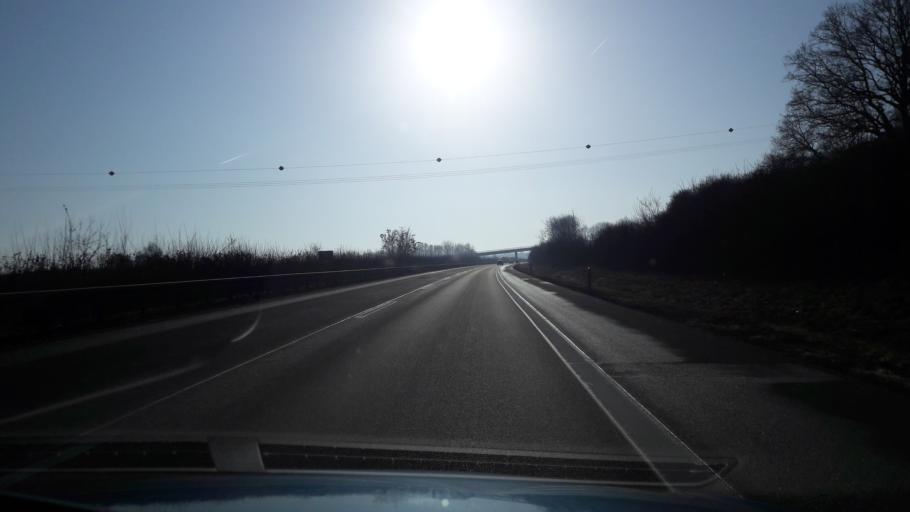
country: DE
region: Hesse
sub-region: Regierungsbezirk Darmstadt
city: Munzenberg
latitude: 50.4545
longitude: 8.7875
